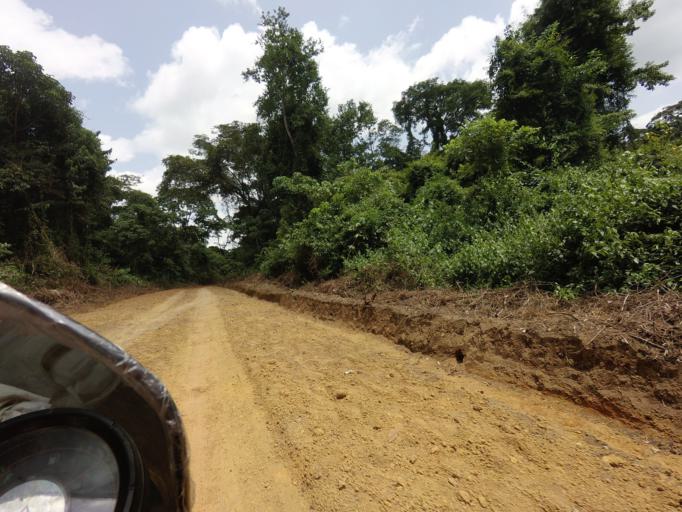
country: SL
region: Eastern Province
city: Tombu
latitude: 8.3744
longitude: -10.7099
